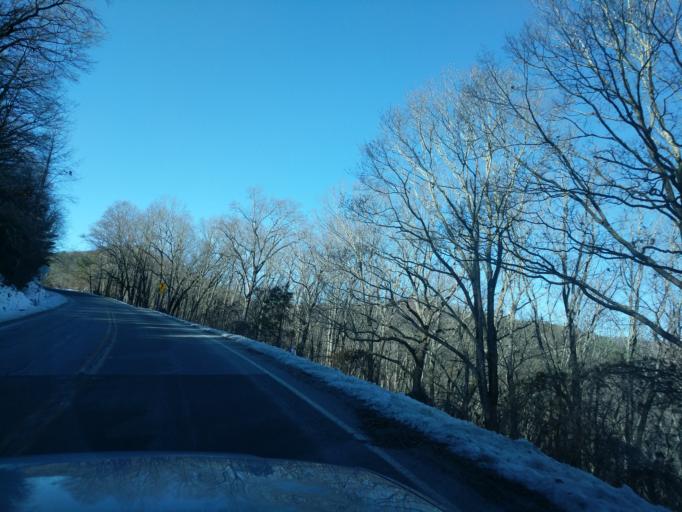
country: US
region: Georgia
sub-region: Rabun County
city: Clayton
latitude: 34.8908
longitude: -83.5833
